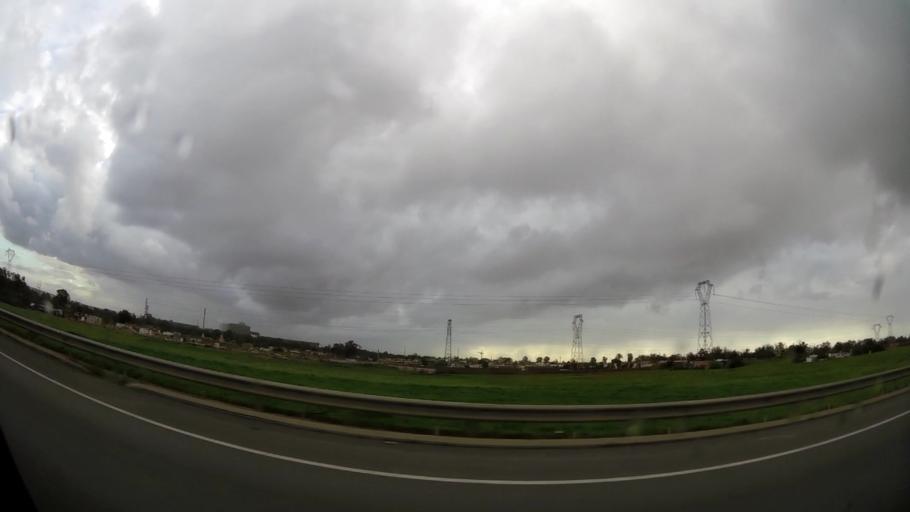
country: MA
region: Grand Casablanca
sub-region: Mohammedia
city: Mohammedia
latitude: 33.6410
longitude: -7.4216
